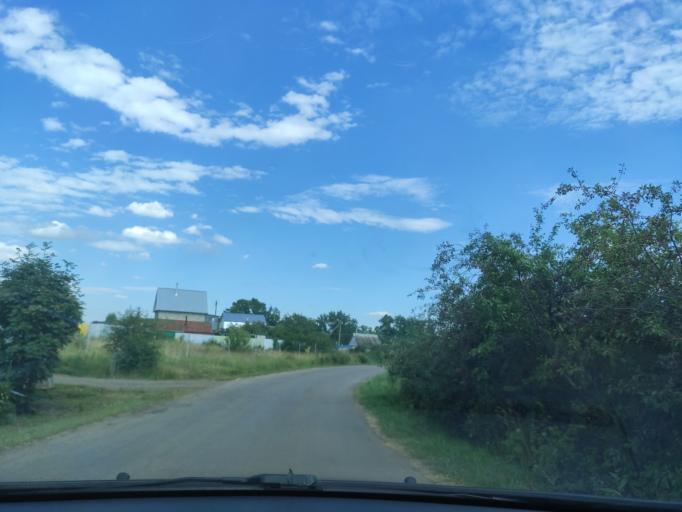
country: RU
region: Ulyanovsk
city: Cherdakly
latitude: 54.4415
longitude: 48.9024
